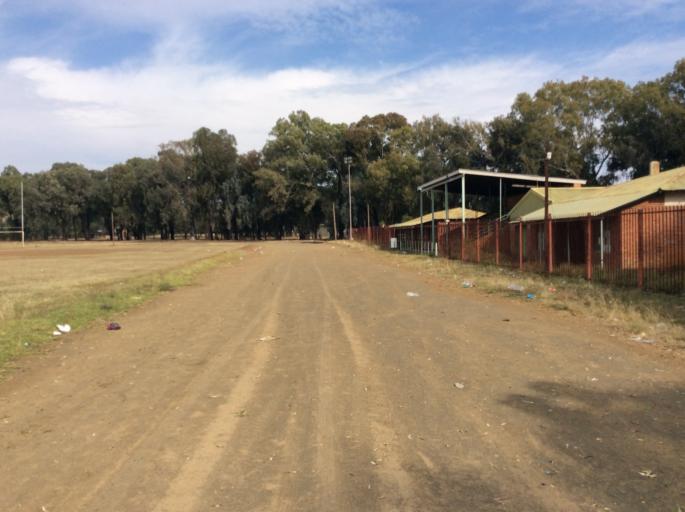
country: ZA
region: Orange Free State
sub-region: Xhariep District Municipality
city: Dewetsdorp
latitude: -29.5781
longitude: 26.6703
